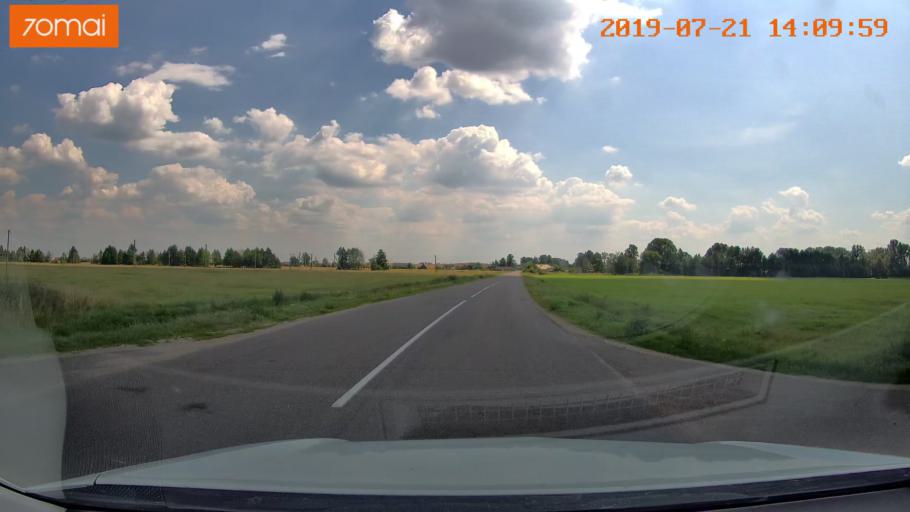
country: BY
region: Grodnenskaya
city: Karelichy
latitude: 53.6673
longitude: 26.1326
